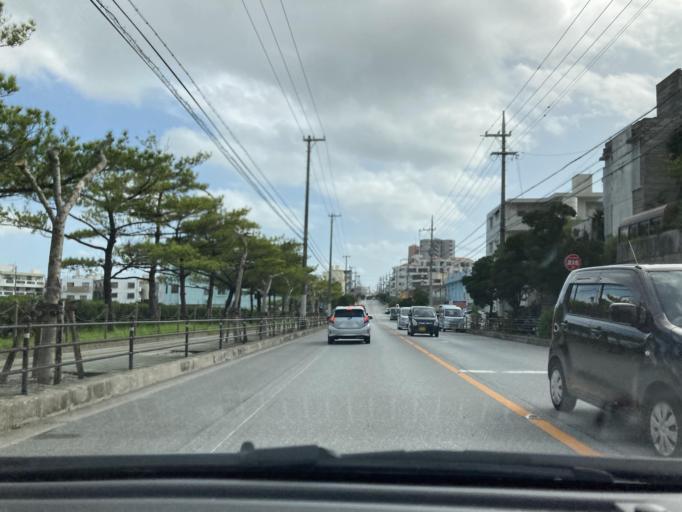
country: JP
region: Okinawa
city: Ginowan
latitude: 26.2620
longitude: 127.7557
